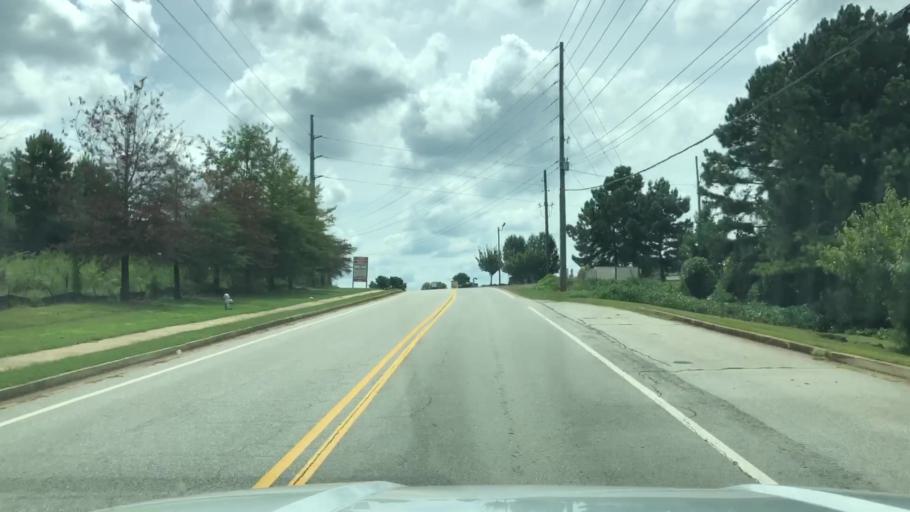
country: US
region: Georgia
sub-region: Gwinnett County
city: Suwanee
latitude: 34.0302
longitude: -84.0447
